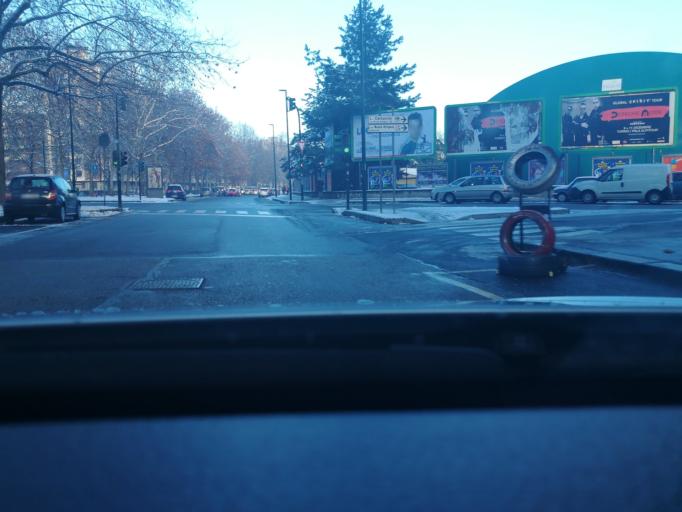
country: IT
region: Piedmont
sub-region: Provincia di Torino
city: Lesna
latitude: 45.0689
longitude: 7.6243
